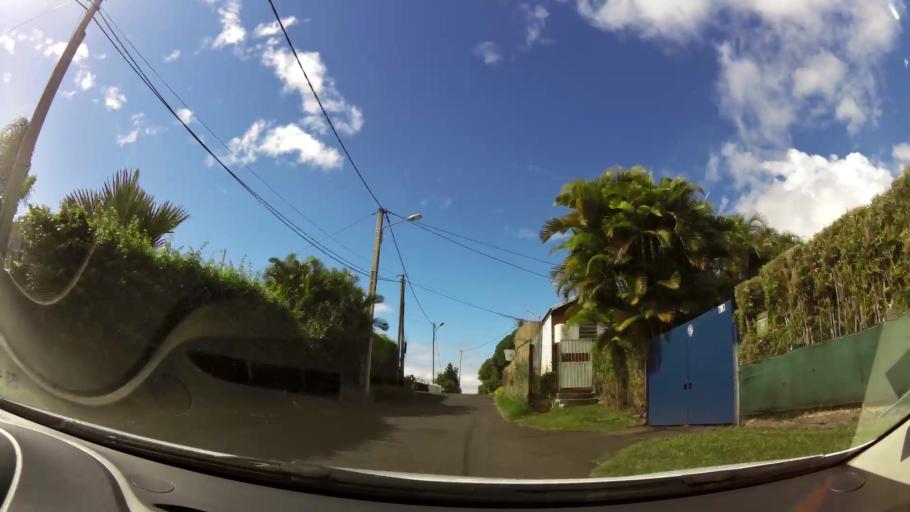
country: RE
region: Reunion
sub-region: Reunion
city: Saint-Denis
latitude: -20.9169
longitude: 55.4927
